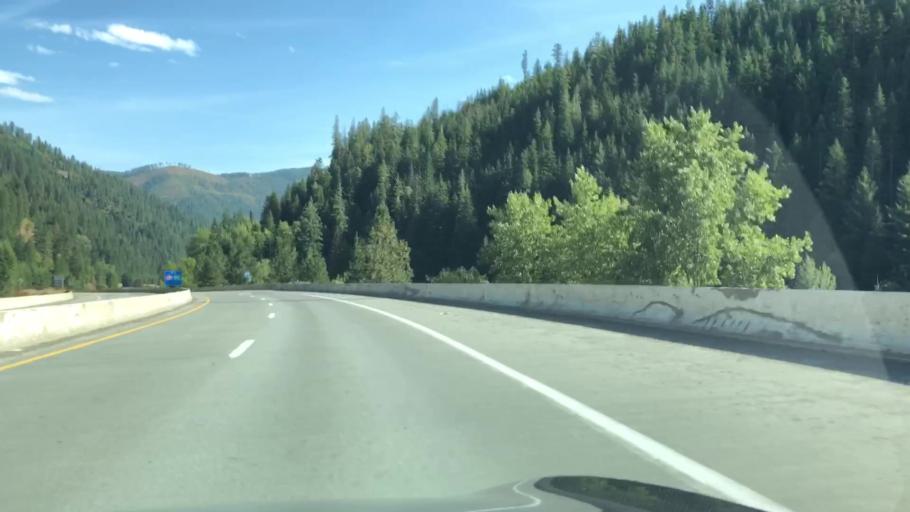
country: US
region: Idaho
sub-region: Shoshone County
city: Wallace
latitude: 47.4886
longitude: -115.9491
